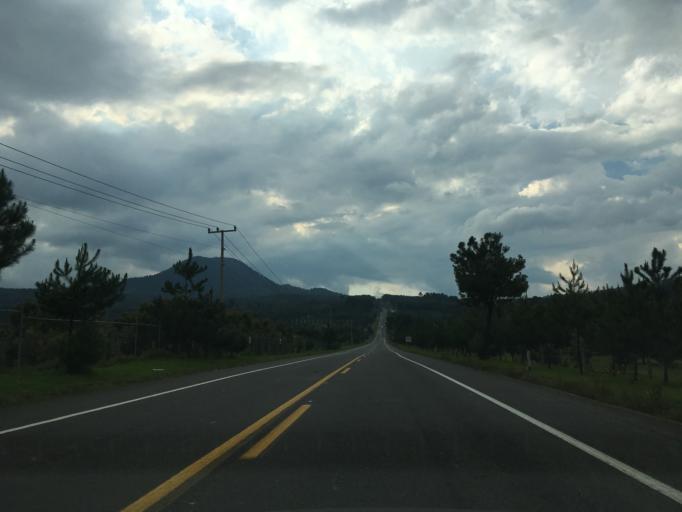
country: MX
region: Michoacan
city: Nuevo San Juan Parangaricutiro
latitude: 19.5053
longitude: -102.1420
